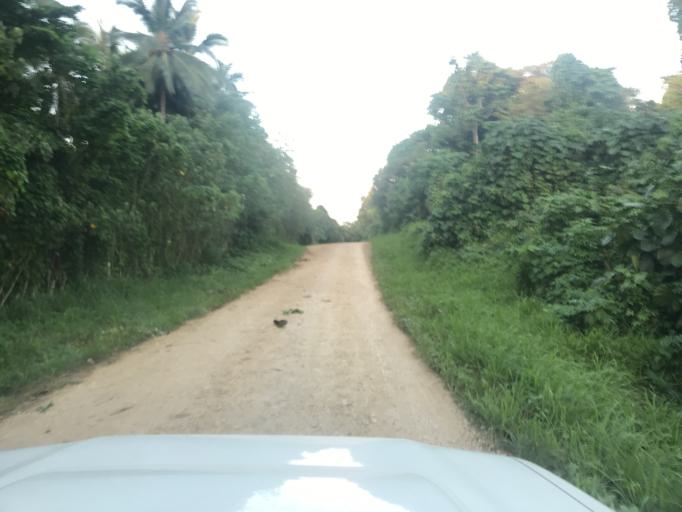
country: VU
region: Sanma
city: Luganville
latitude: -15.5611
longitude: 166.9622
